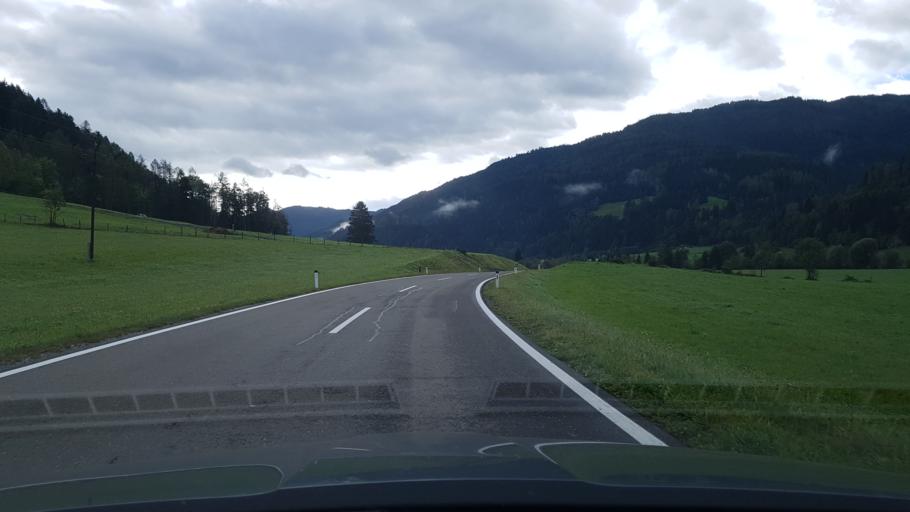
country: AT
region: Styria
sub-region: Politischer Bezirk Murau
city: Winklern bei Oberwolz
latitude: 47.1743
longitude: 14.2343
